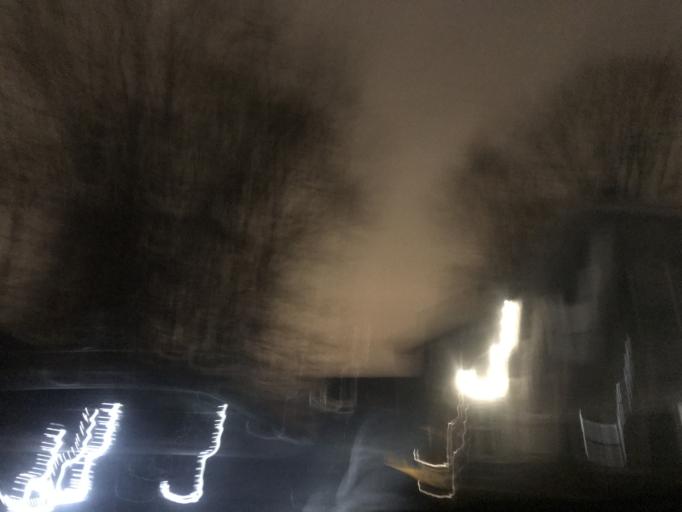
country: US
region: Maryland
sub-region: Prince George's County
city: Oxon Hill
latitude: 38.8027
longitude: -76.9733
